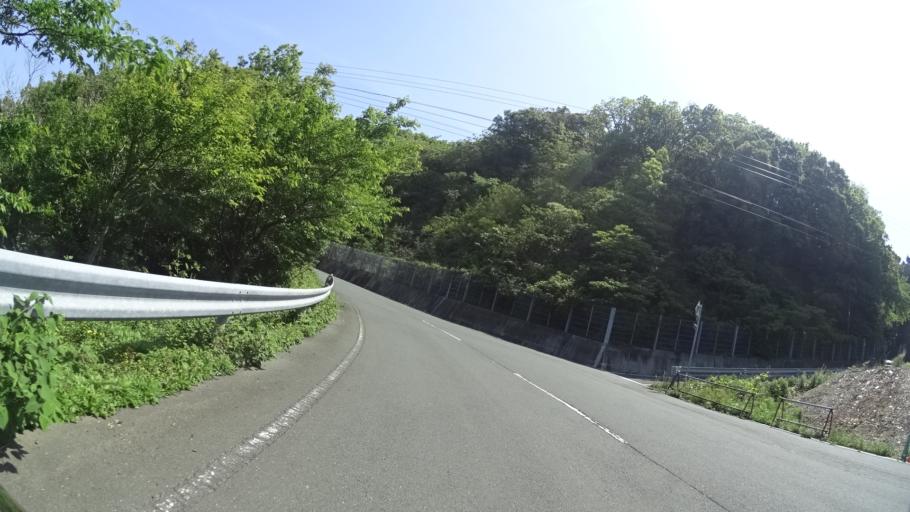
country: JP
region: Oita
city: Tsukumiura
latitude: 33.3592
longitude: 132.0392
